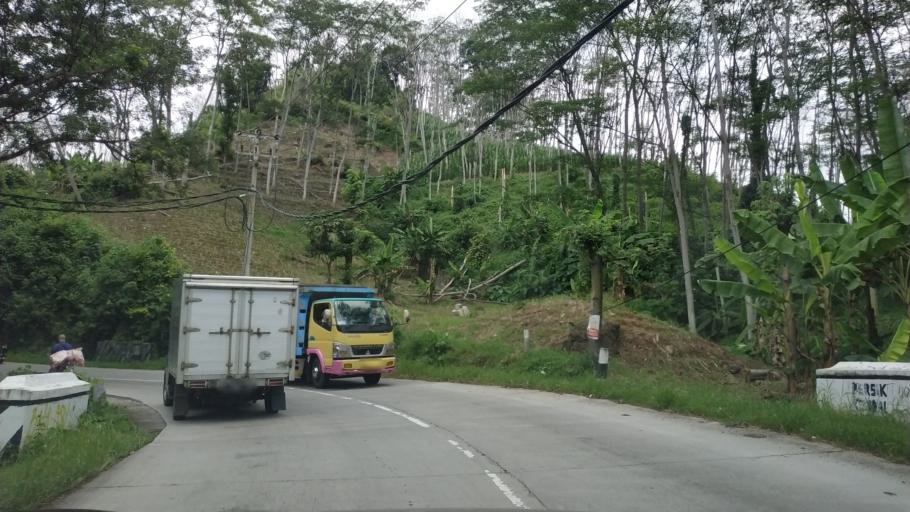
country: ID
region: Central Java
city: Weleri
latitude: -7.0039
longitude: 110.0596
